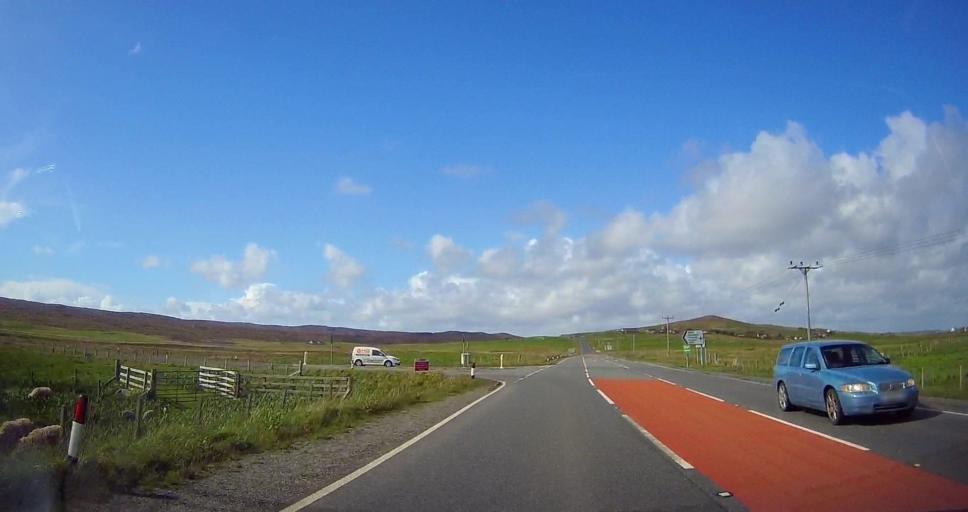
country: GB
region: Scotland
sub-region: Shetland Islands
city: Lerwick
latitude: 60.1901
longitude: -1.2323
